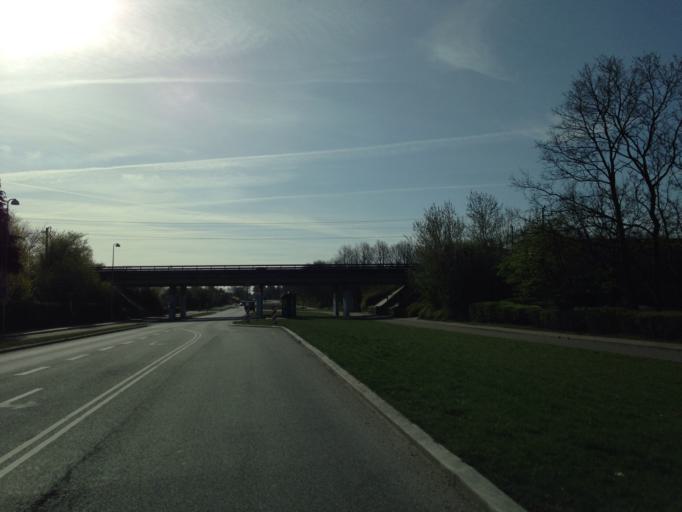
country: DK
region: Zealand
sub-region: Greve Kommune
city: Greve
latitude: 55.5831
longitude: 12.2973
